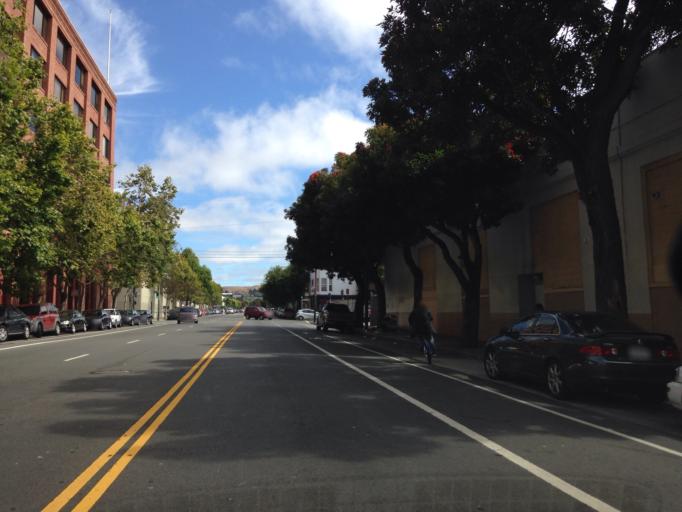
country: US
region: California
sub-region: San Francisco County
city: San Francisco
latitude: 37.7678
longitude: -122.4155
